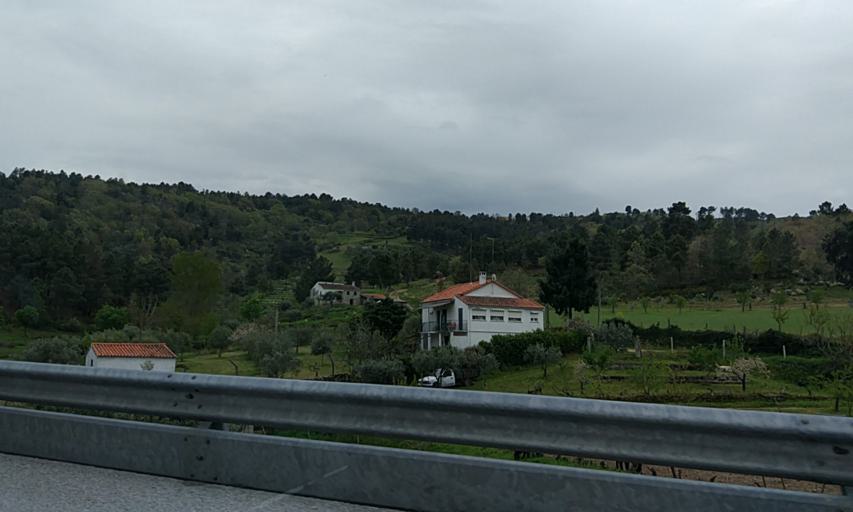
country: PT
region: Guarda
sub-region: Celorico da Beira
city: Celorico da Beira
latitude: 40.6268
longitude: -7.3812
